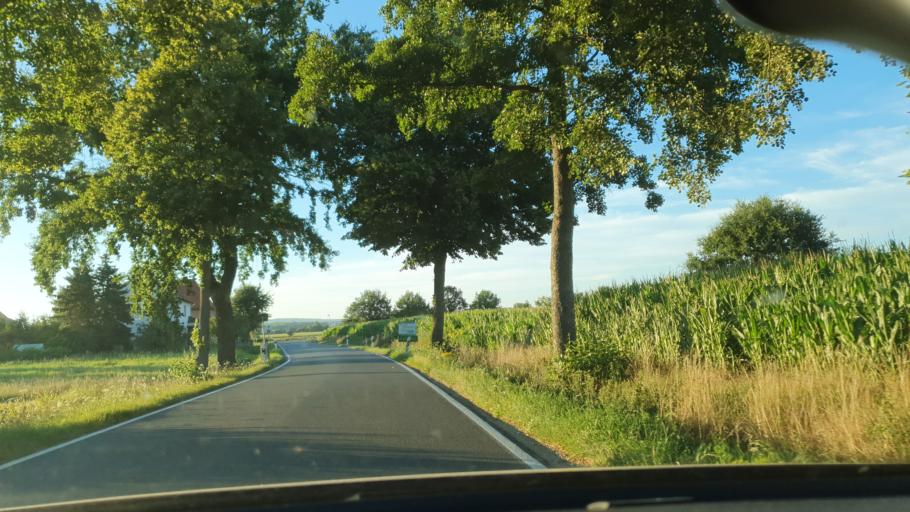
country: DE
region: North Rhine-Westphalia
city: Spenge
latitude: 52.1820
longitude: 8.5122
